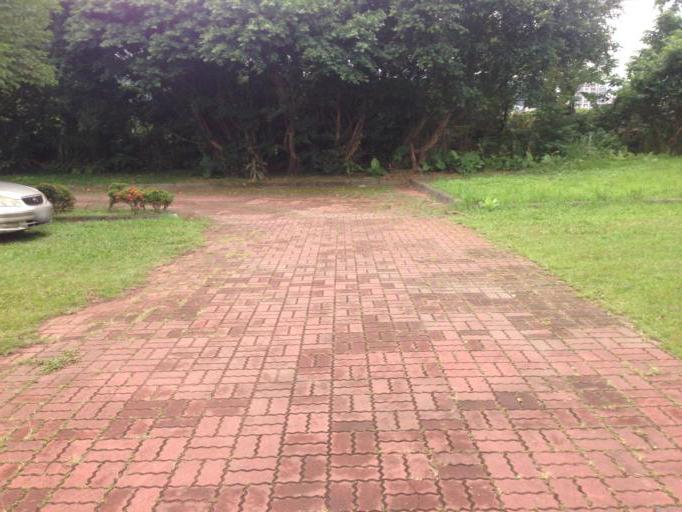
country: TW
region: Taiwan
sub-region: Taoyuan
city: Taoyuan
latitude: 24.9362
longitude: 121.3813
